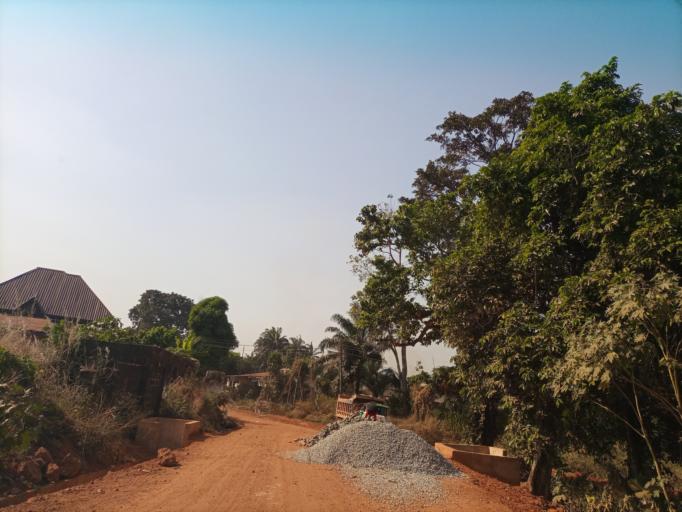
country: NG
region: Enugu
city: Aku
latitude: 6.7057
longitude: 7.3121
